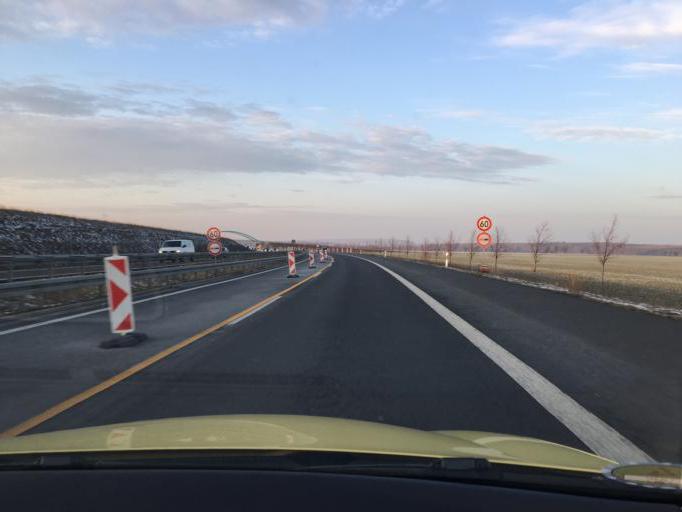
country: DE
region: Saxony
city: Borna
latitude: 51.1257
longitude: 12.5185
